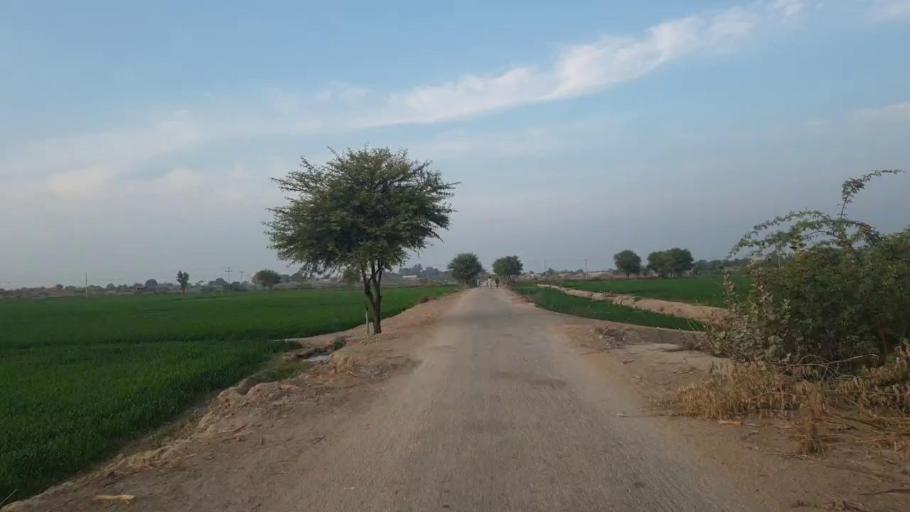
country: PK
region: Sindh
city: Shahpur Chakar
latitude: 26.1164
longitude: 68.5465
